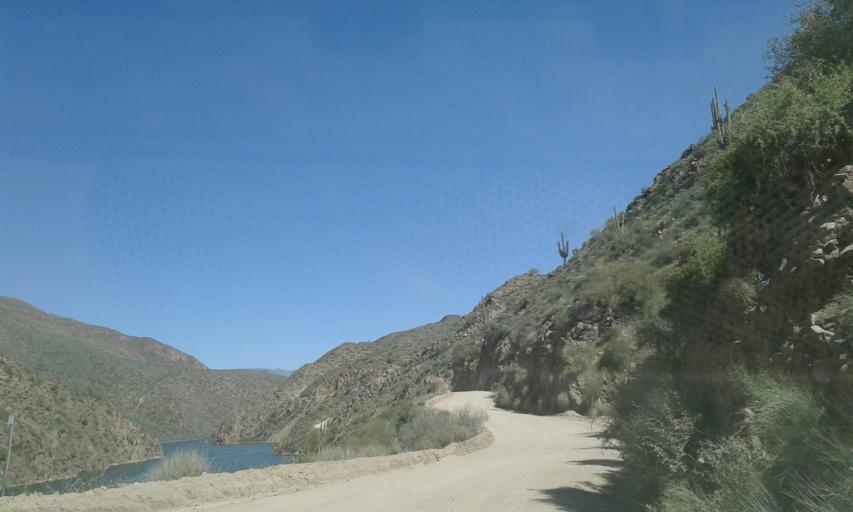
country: US
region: Arizona
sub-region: Gila County
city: Tonto Basin
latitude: 33.6495
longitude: -111.1899
